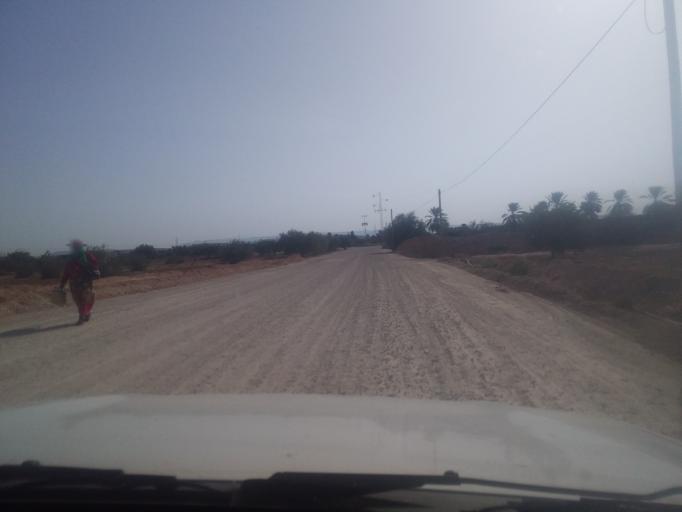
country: TN
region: Qabis
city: Matmata
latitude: 33.5990
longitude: 10.2748
